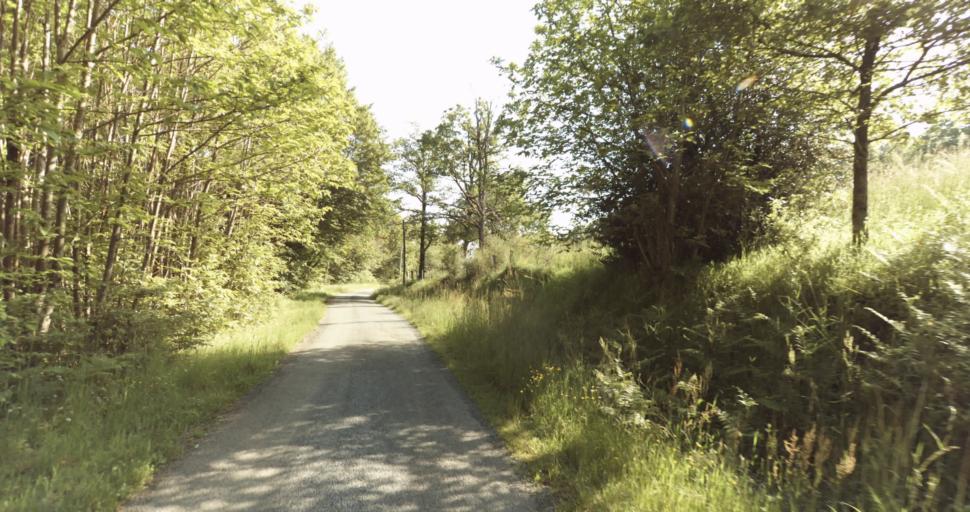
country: FR
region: Limousin
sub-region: Departement de la Haute-Vienne
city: Solignac
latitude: 45.7336
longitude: 1.2434
